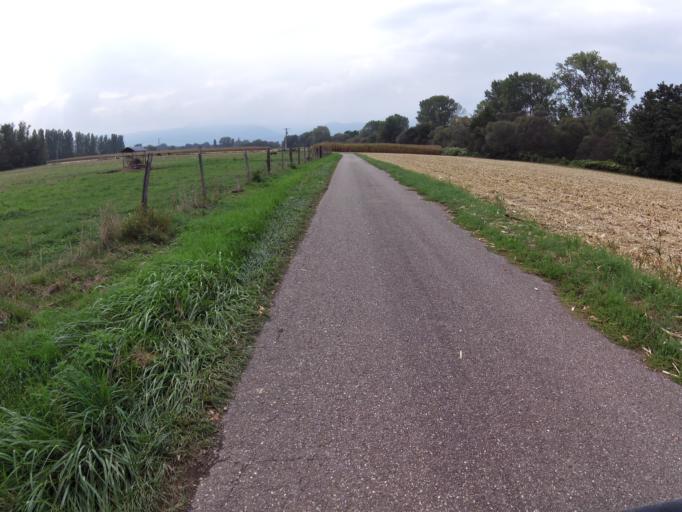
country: FR
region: Alsace
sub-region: Departement du Haut-Rhin
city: Guemar
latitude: 48.1862
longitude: 7.4168
